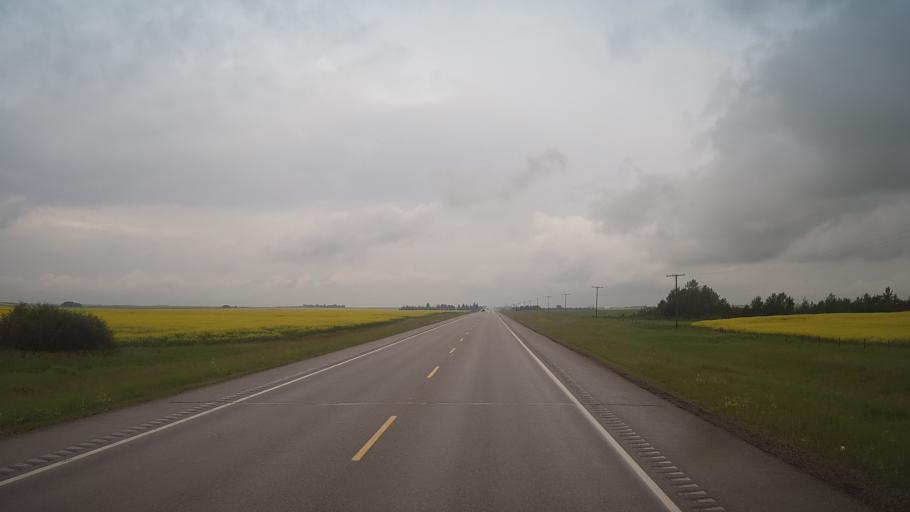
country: CA
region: Saskatchewan
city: Unity
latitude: 52.4349
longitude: -109.0104
